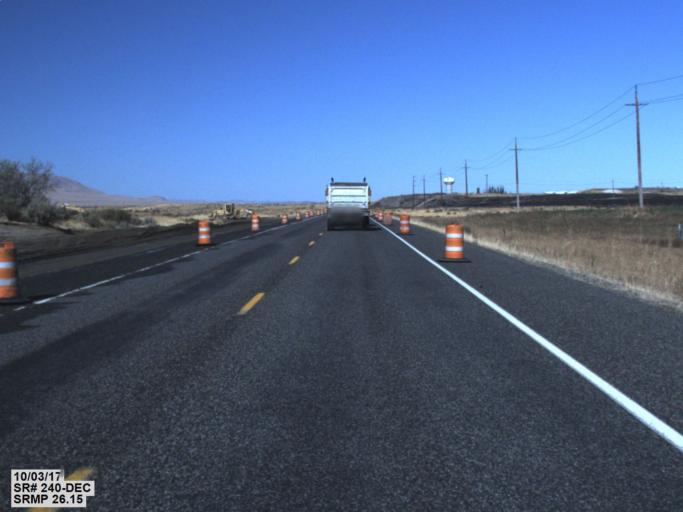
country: US
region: Washington
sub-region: Benton County
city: West Richland
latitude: 46.3324
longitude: -119.3295
